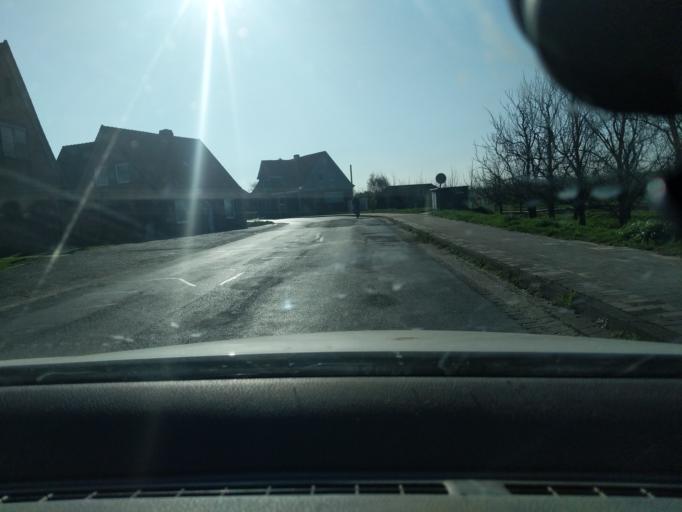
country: DE
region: Lower Saxony
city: Grunendeich
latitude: 53.5651
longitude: 9.6341
